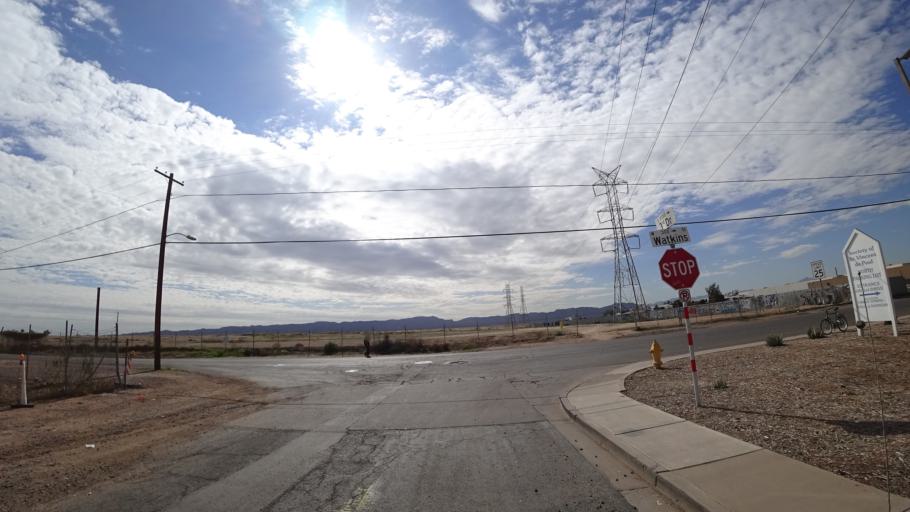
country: US
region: Arizona
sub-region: Maricopa County
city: Phoenix
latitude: 33.4261
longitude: -112.0783
